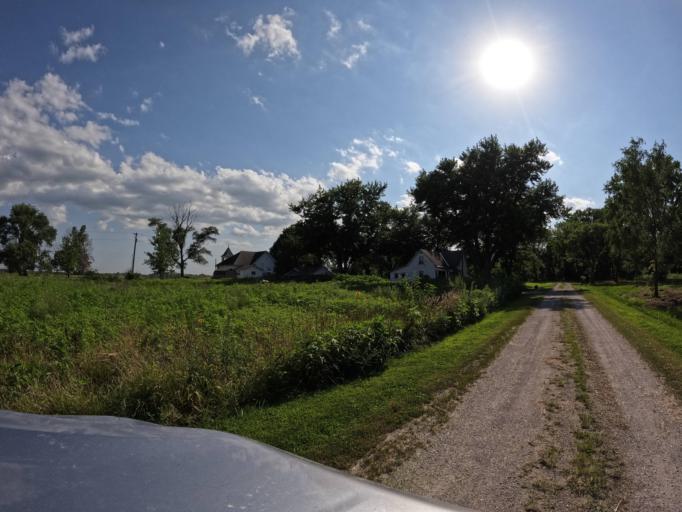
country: US
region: Iowa
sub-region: Appanoose County
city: Centerville
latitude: 40.7188
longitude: -93.0323
